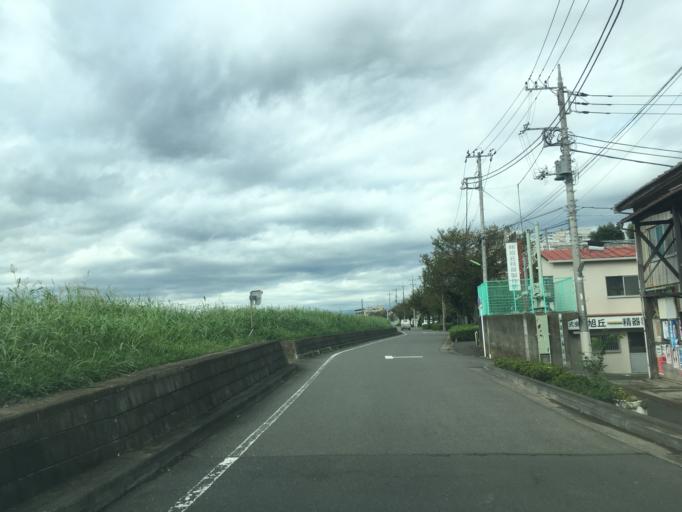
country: JP
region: Tokyo
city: Chofugaoka
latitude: 35.6193
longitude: 139.6015
